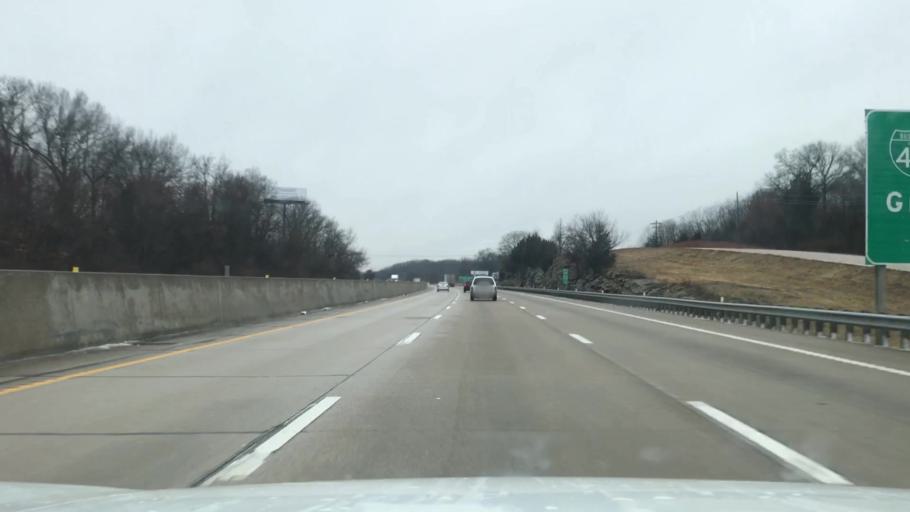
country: US
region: Missouri
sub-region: Franklin County
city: Gray Summit
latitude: 38.4883
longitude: -90.8020
